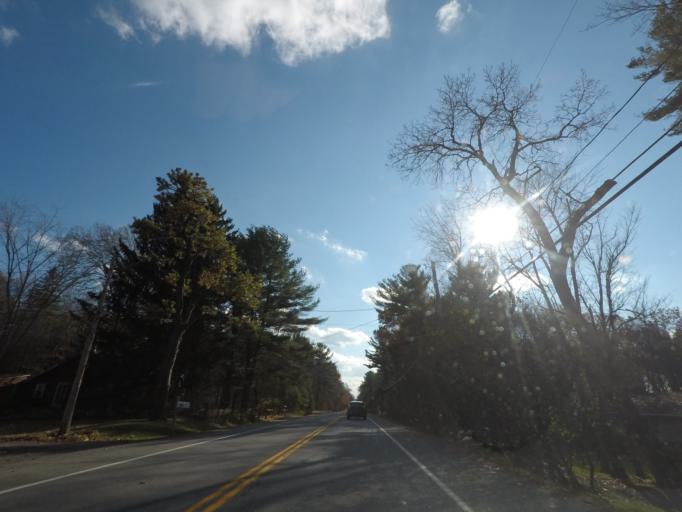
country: US
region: New York
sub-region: Schenectady County
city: East Glenville
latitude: 42.8728
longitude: -73.8876
